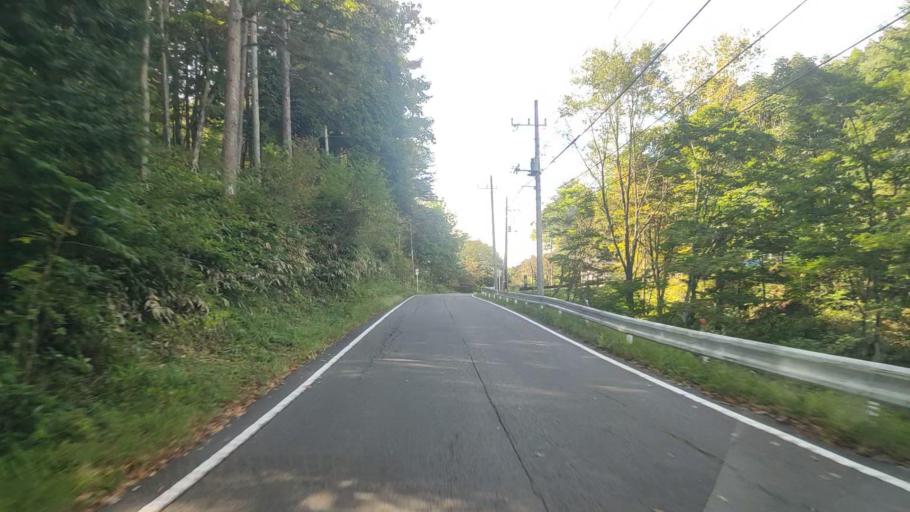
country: JP
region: Gunma
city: Nakanojomachi
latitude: 36.6036
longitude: 138.6845
